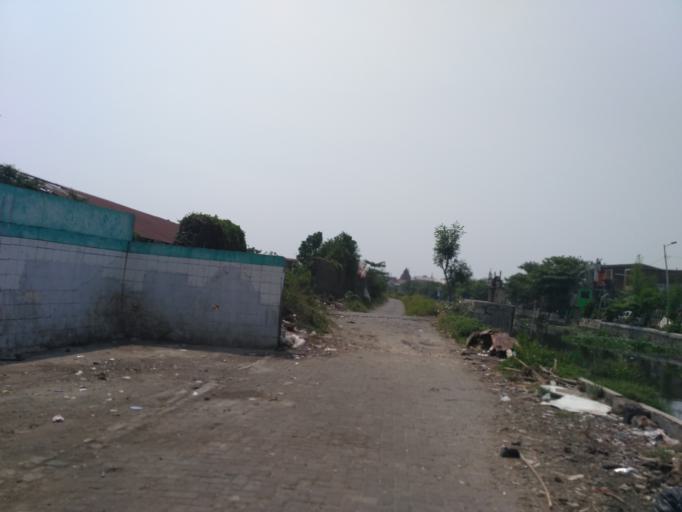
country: ID
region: Central Java
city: Semarang
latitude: -6.9650
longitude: 110.4403
